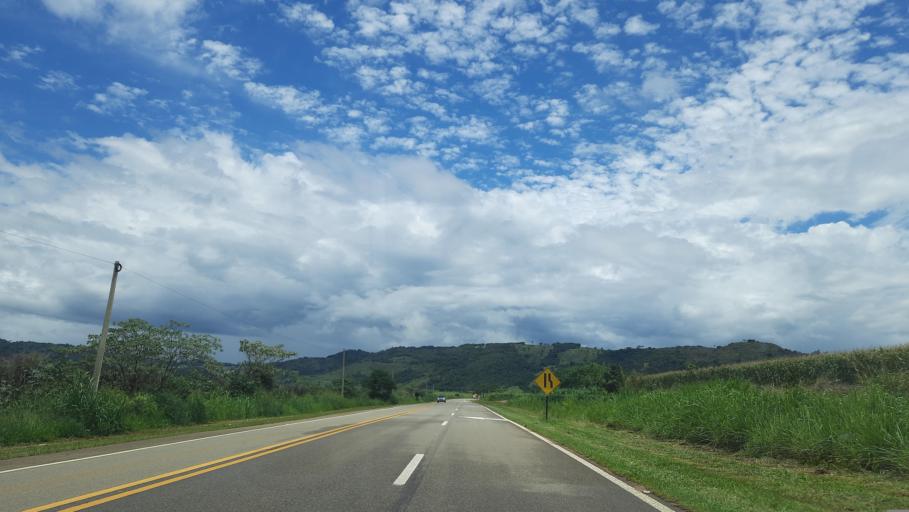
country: BR
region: Sao Paulo
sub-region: Vargem Grande Do Sul
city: Vargem Grande do Sul
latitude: -21.8123
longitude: -46.7878
